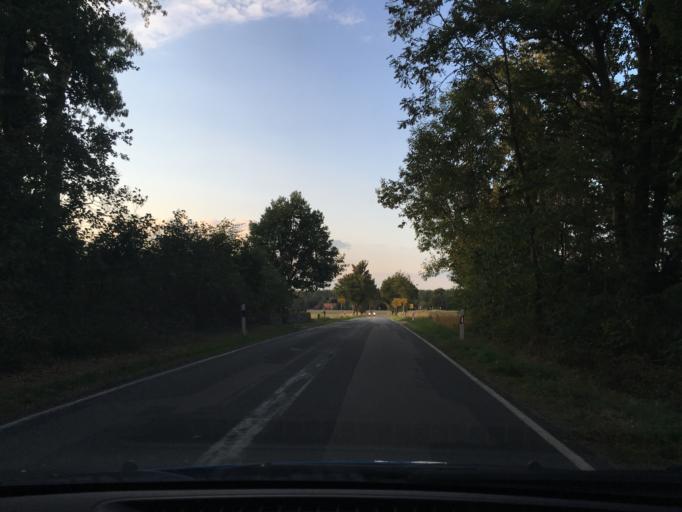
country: DE
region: Lower Saxony
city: Dahlem
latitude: 53.2297
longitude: 10.7560
